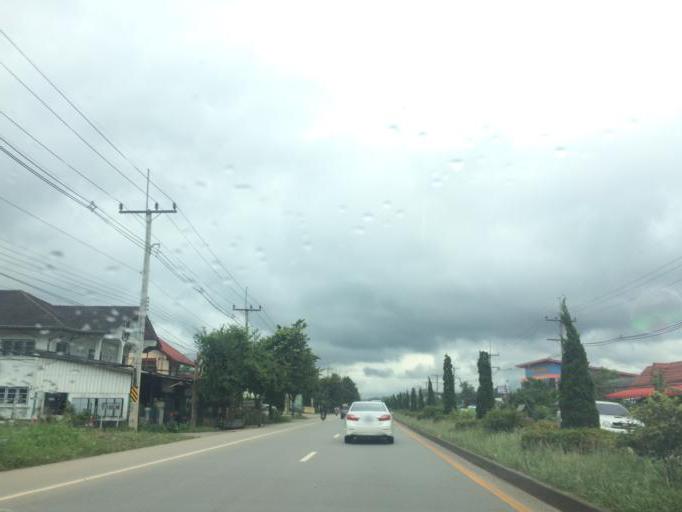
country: TH
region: Chiang Rai
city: Chiang Rai
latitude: 20.0240
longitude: 99.8719
